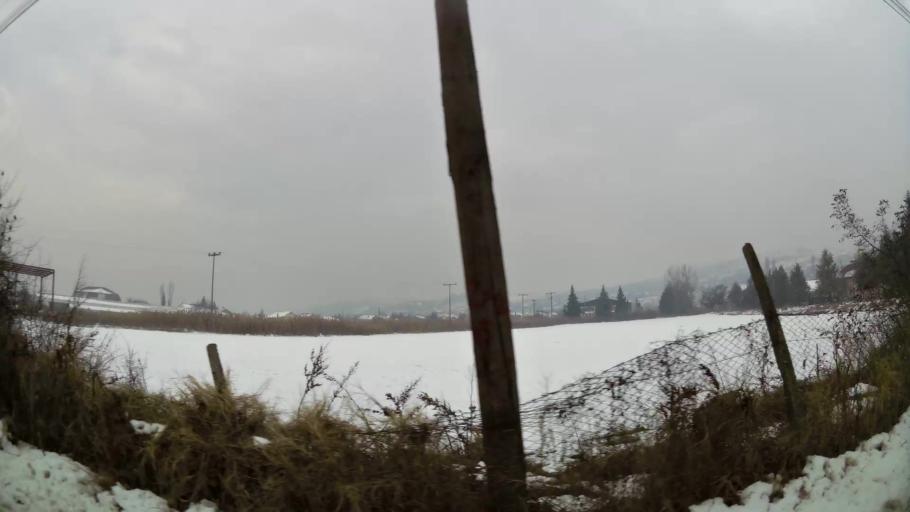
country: MK
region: Saraj
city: Saraj
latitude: 42.0311
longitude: 21.3437
